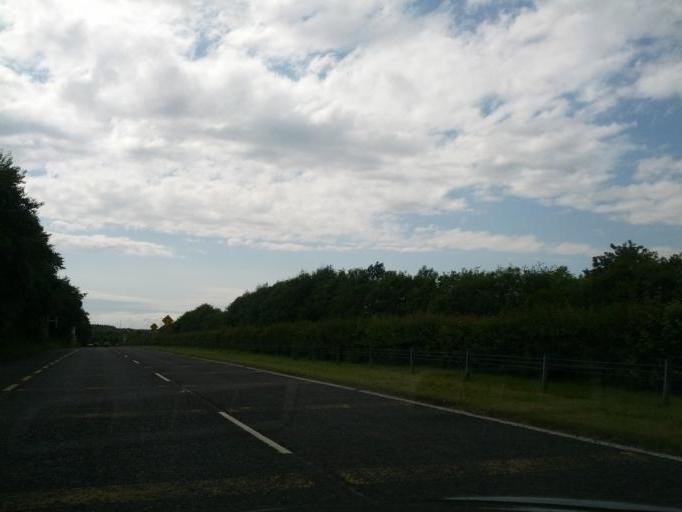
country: IE
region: Connaught
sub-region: County Galway
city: Oranmore
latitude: 53.2790
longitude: -8.9672
